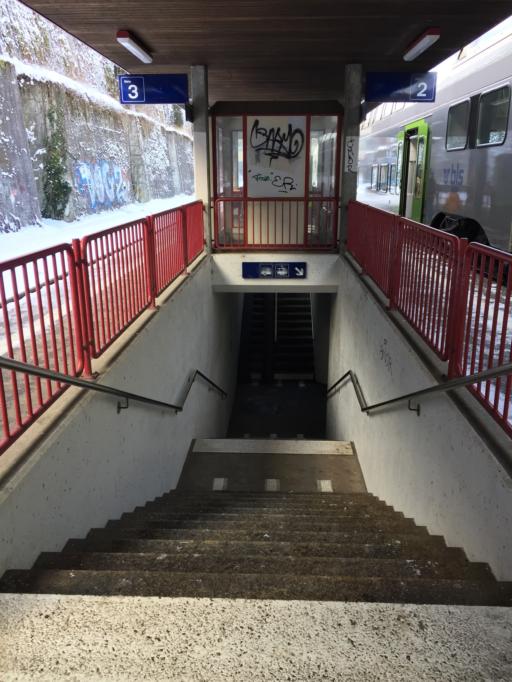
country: CH
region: Bern
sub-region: Bern-Mittelland District
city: Bern
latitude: 46.9284
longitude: 7.4463
